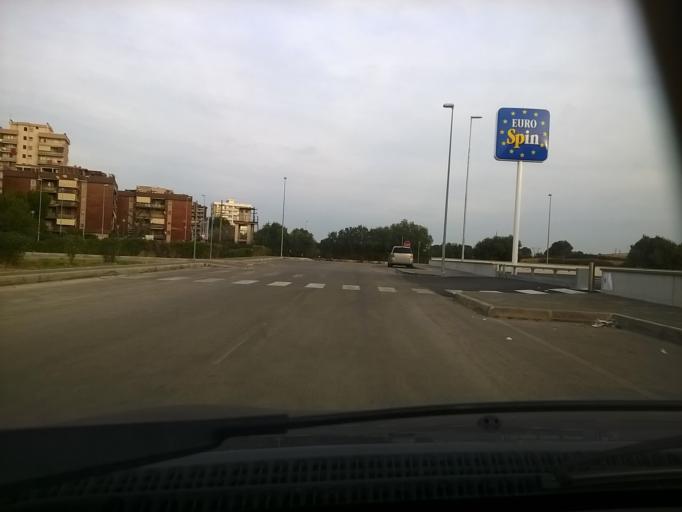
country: IT
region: Apulia
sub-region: Provincia di Taranto
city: Taranto
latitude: 40.4324
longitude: 17.2631
